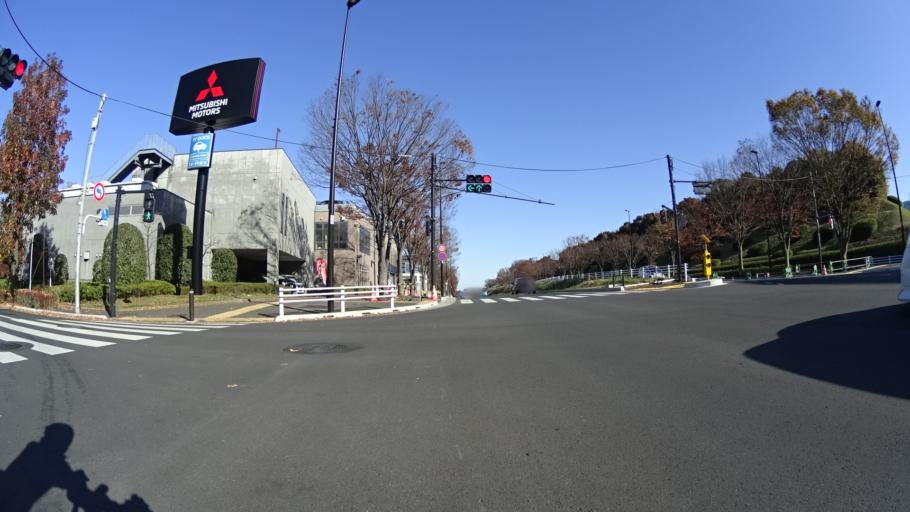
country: JP
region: Tokyo
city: Hino
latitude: 35.6130
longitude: 139.4017
